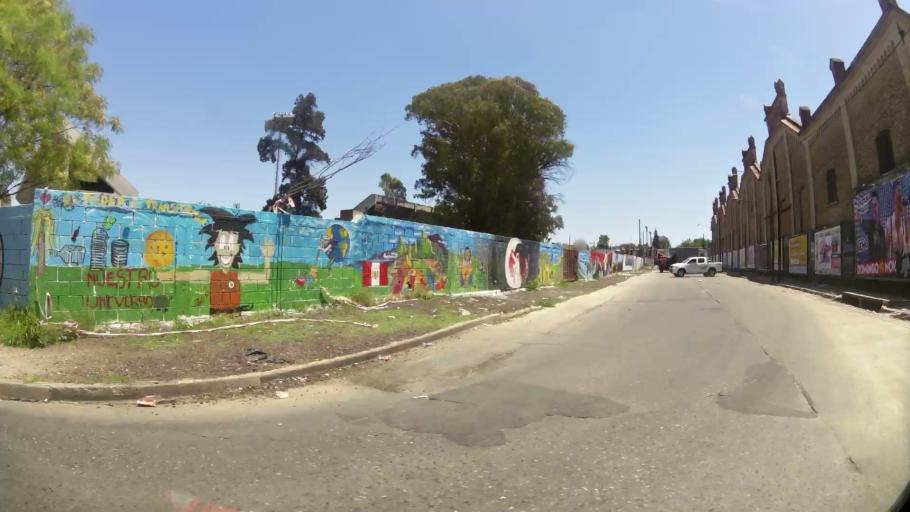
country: AR
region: Cordoba
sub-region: Departamento de Capital
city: Cordoba
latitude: -31.4027
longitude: -64.2051
